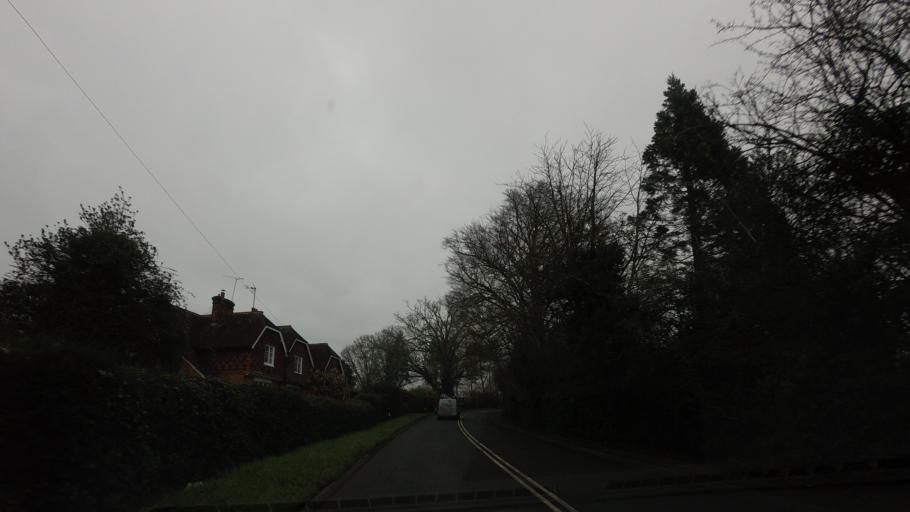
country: GB
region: England
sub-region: Kent
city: Hawkhurst
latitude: 51.0591
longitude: 0.5053
